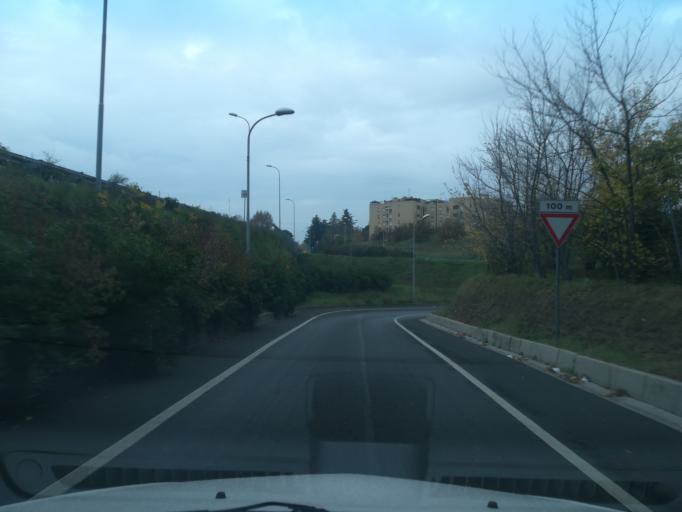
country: IT
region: Emilia-Romagna
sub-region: Provincia di Bologna
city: Imola
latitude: 44.3638
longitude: 11.6991
